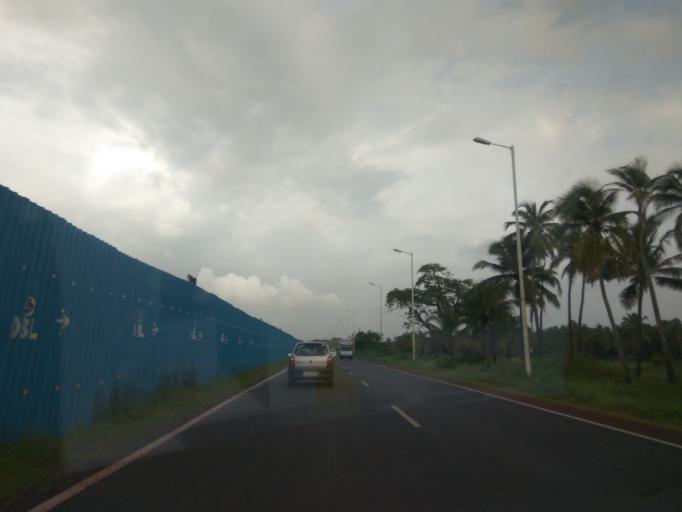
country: IN
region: Goa
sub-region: North Goa
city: Goa Velha
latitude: 15.4317
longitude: 73.8884
